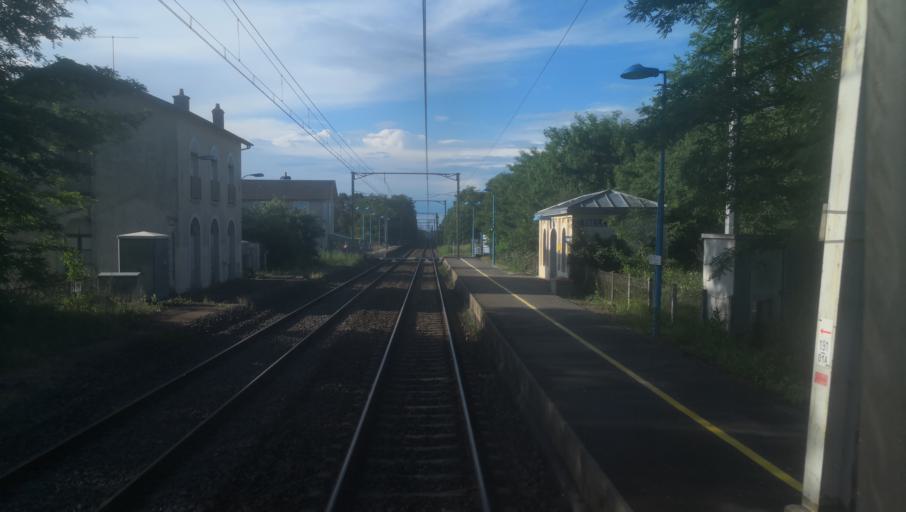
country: FR
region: Centre
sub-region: Departement du Loir-et-Cher
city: Theillay
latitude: 47.3136
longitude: 2.0445
